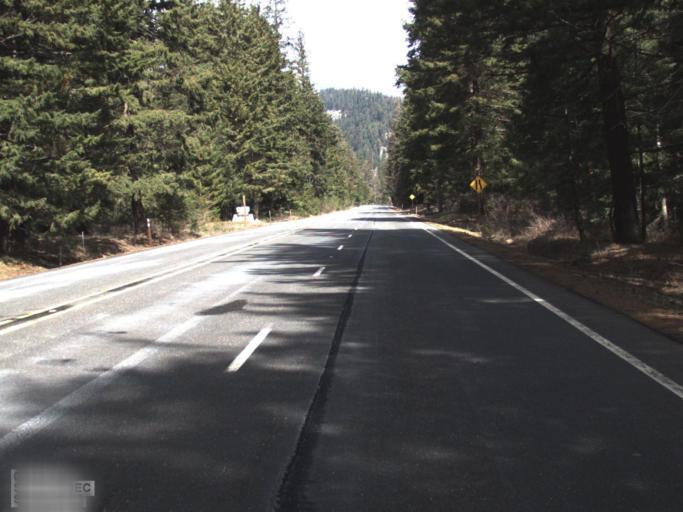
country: US
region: Washington
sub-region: Kittitas County
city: Cle Elum
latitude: 46.9735
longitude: -121.0949
